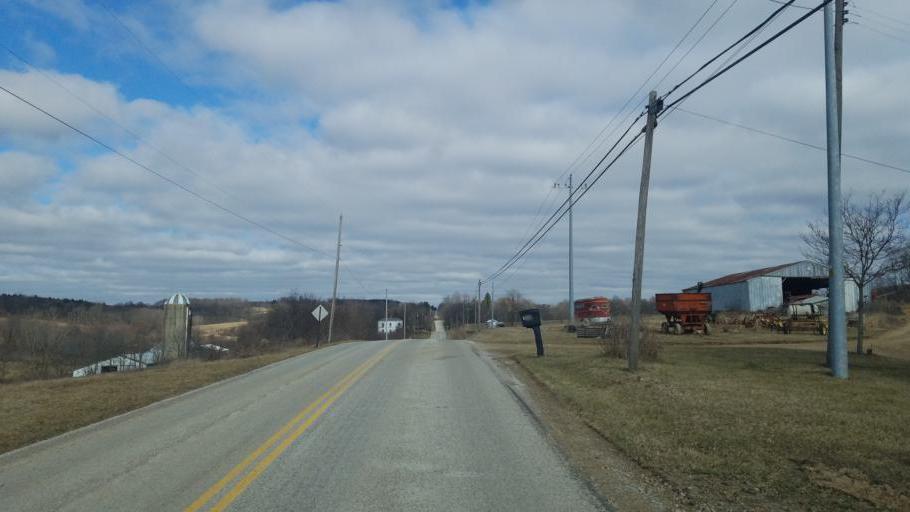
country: US
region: Ohio
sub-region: Sandusky County
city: Bellville
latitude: 40.5598
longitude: -82.5094
